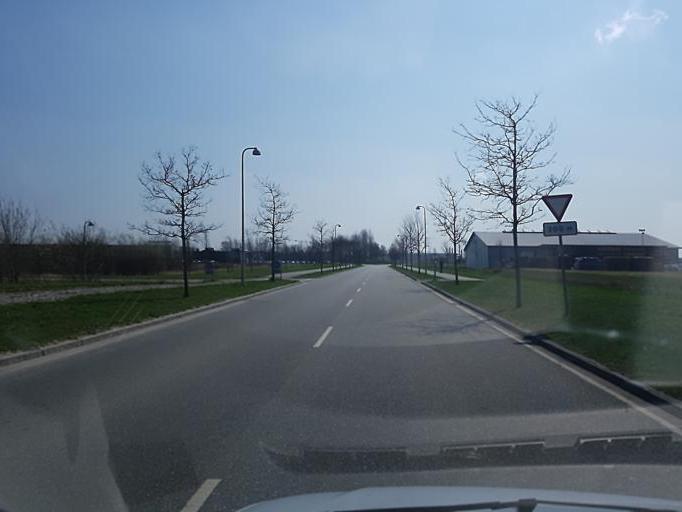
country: DK
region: South Denmark
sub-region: Odense Kommune
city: Neder Holluf
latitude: 55.3742
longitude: 10.4848
